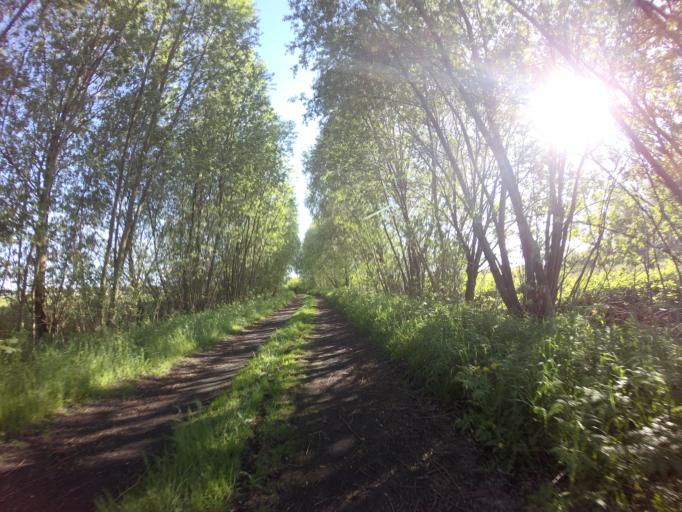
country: PL
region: West Pomeranian Voivodeship
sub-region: Powiat choszczenski
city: Pelczyce
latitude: 53.1257
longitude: 15.3238
